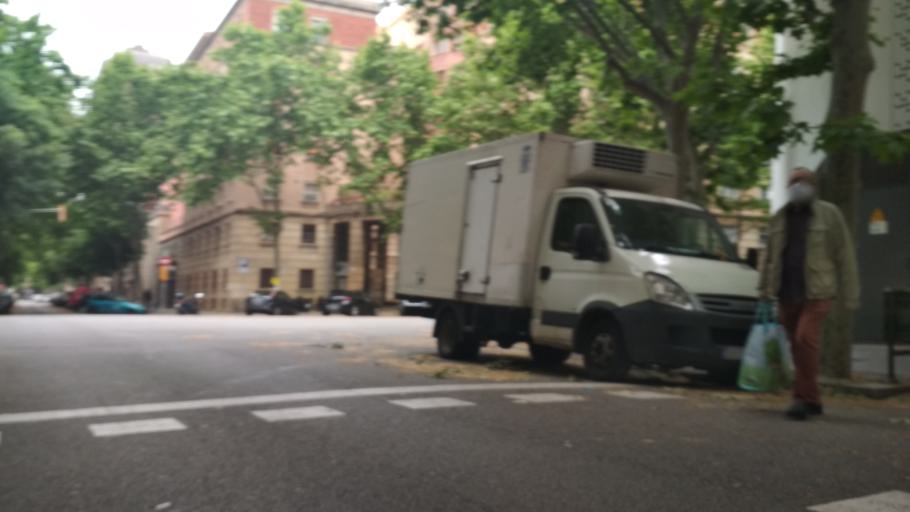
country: ES
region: Catalonia
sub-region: Provincia de Barcelona
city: Sant Marti
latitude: 41.4173
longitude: 2.2029
